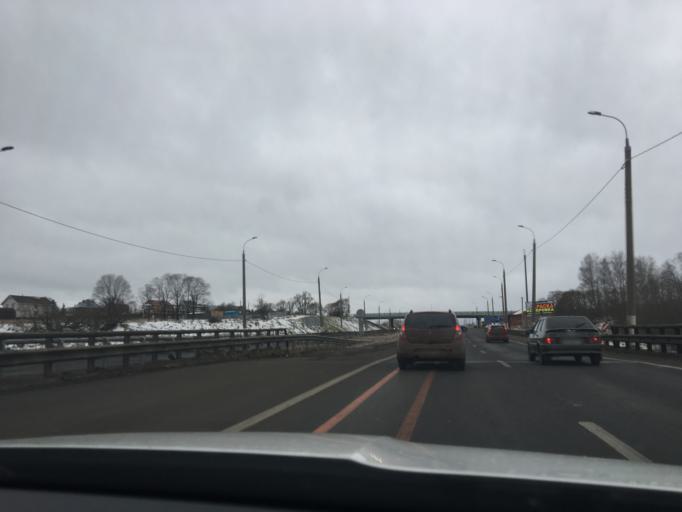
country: RU
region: Moskovskaya
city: Serpukhov
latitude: 54.8571
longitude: 37.4808
